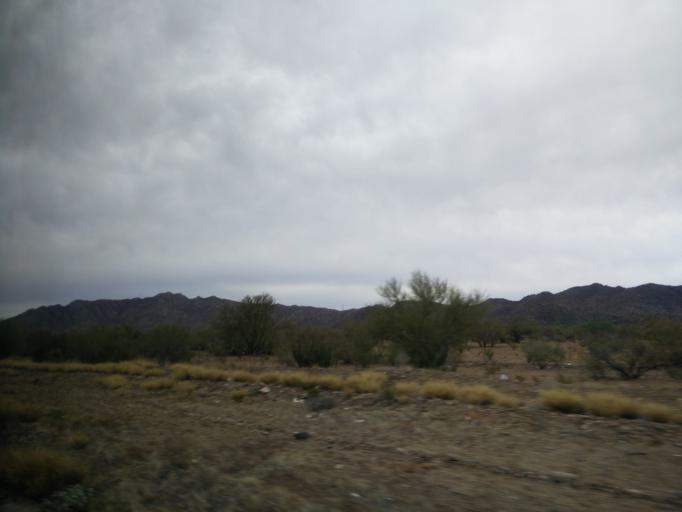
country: MX
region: Sonora
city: Hermosillo
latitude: 28.9467
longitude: -110.9621
